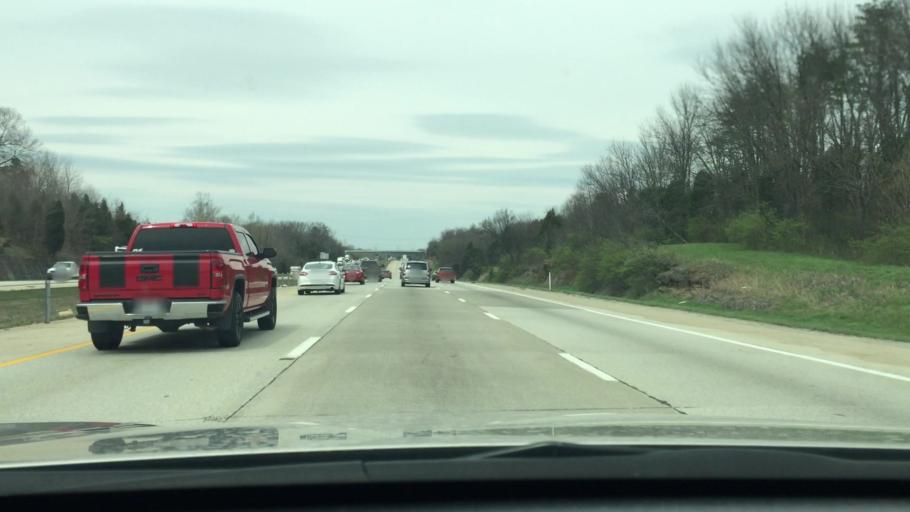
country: US
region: Kentucky
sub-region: Bullitt County
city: Shepherdsville
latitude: 38.0152
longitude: -85.6964
